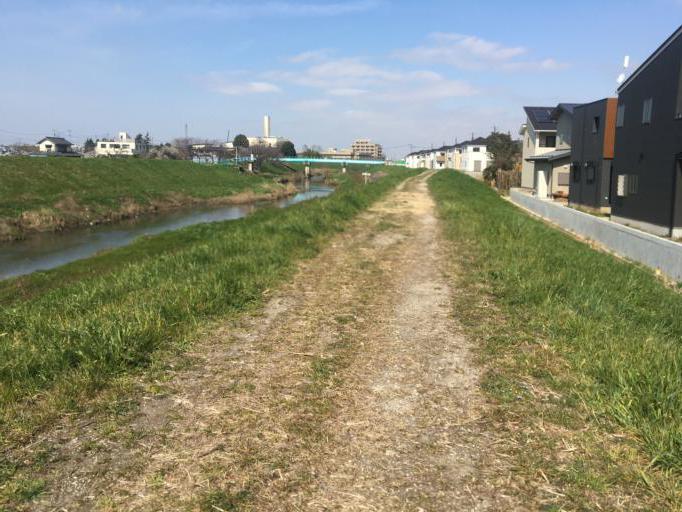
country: JP
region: Saitama
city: Oi
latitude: 35.8652
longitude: 139.5516
